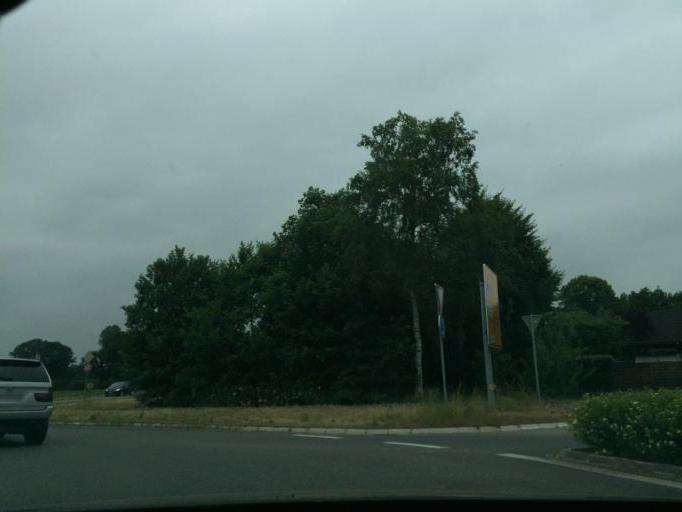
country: DE
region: North Rhine-Westphalia
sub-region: Regierungsbezirk Munster
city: Ostbevern
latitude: 52.1156
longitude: 7.8526
